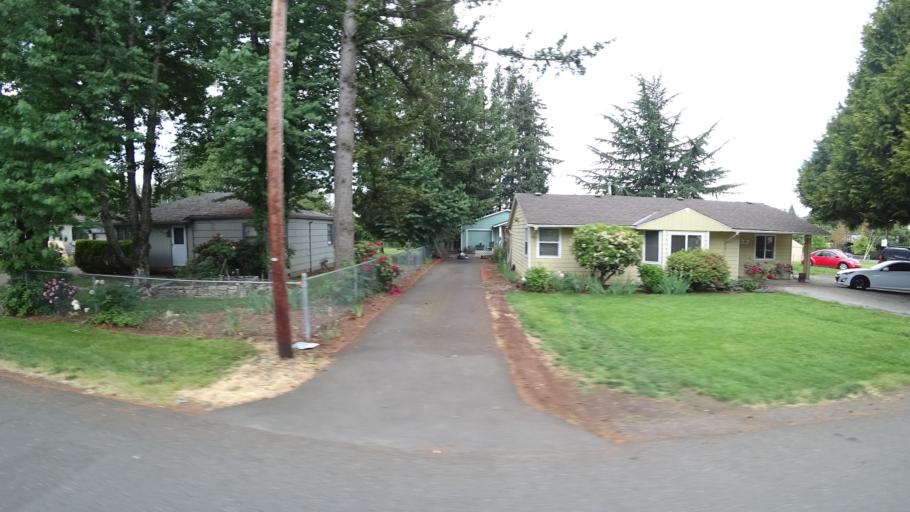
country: US
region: Oregon
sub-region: Clackamas County
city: Happy Valley
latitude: 45.5038
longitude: -122.5060
